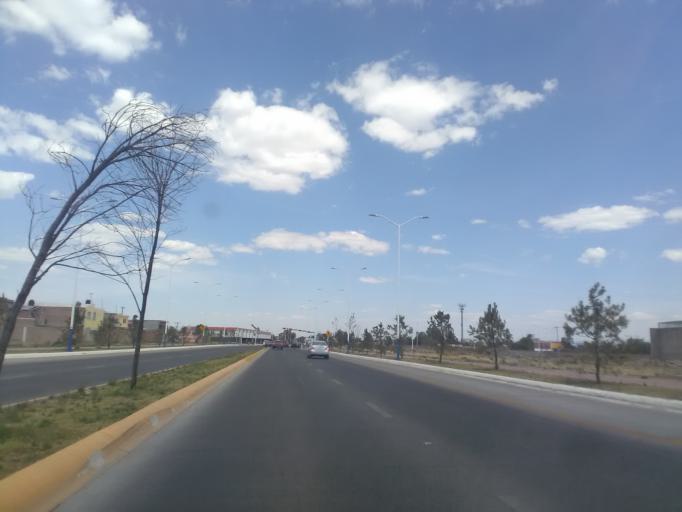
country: MX
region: Durango
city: Victoria de Durango
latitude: 24.0371
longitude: -104.6624
